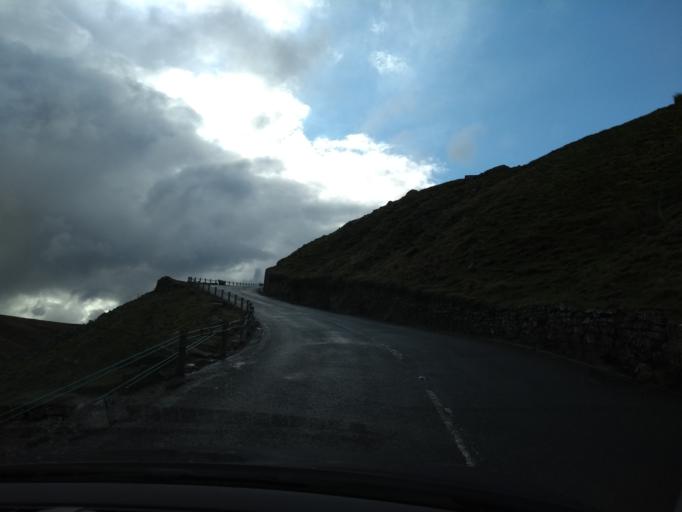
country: GB
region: England
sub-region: Cumbria
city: Kirkby Stephen
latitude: 54.3591
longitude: -2.1981
